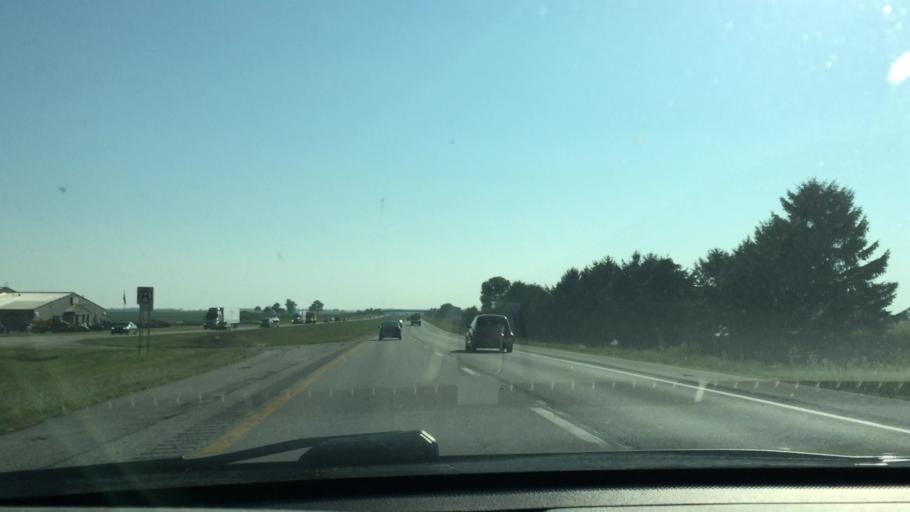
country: US
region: Ohio
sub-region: Greene County
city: Jamestown
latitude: 39.5532
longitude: -83.7302
